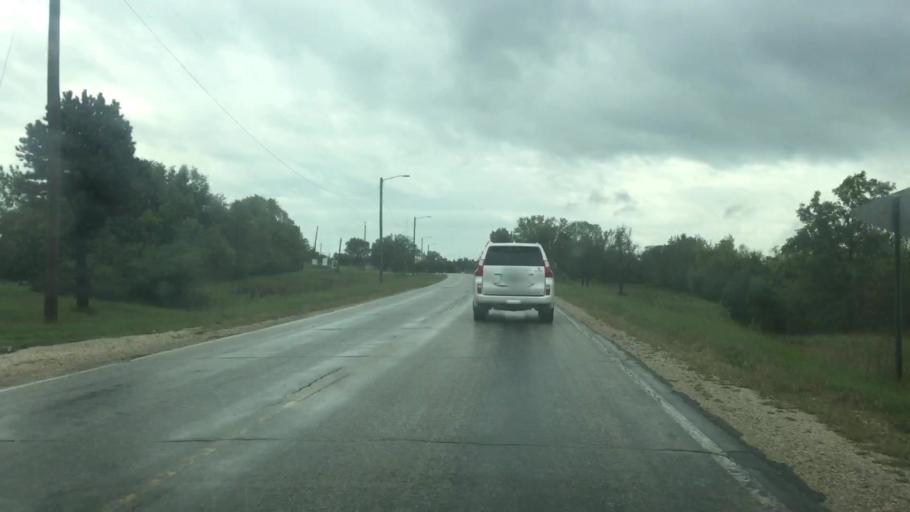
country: US
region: Kansas
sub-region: Allen County
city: Iola
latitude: 37.9059
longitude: -95.4098
